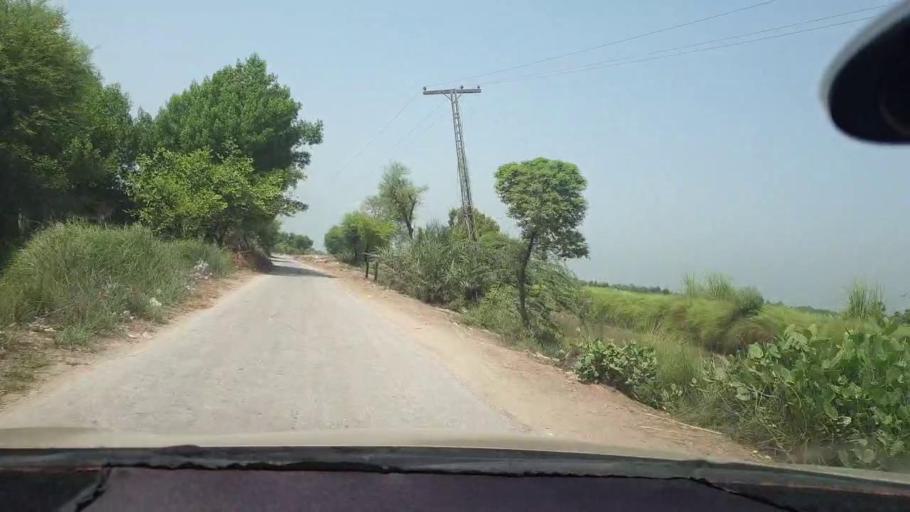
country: PK
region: Sindh
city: Kambar
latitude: 27.6359
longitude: 67.9807
